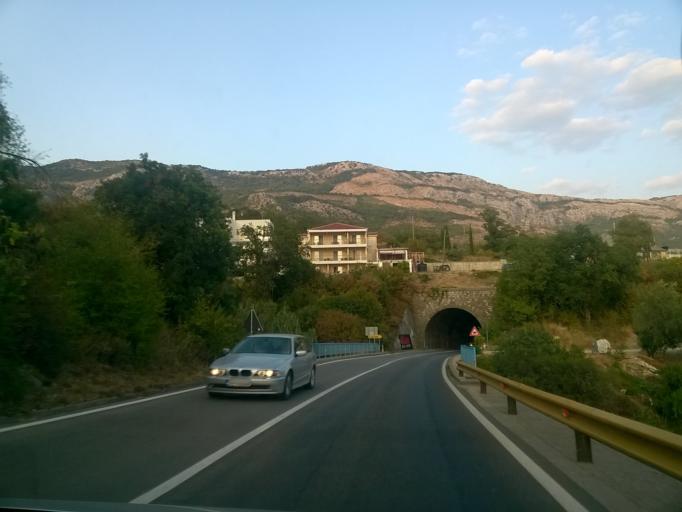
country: ME
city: Petrovac na Moru
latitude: 42.2039
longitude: 18.9550
